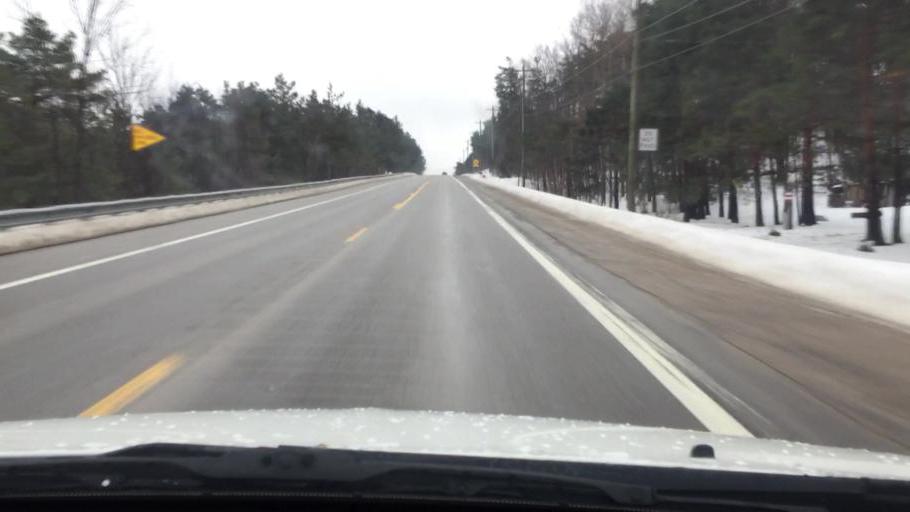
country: US
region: Michigan
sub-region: Charlevoix County
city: Charlevoix
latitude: 45.2680
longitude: -85.2063
